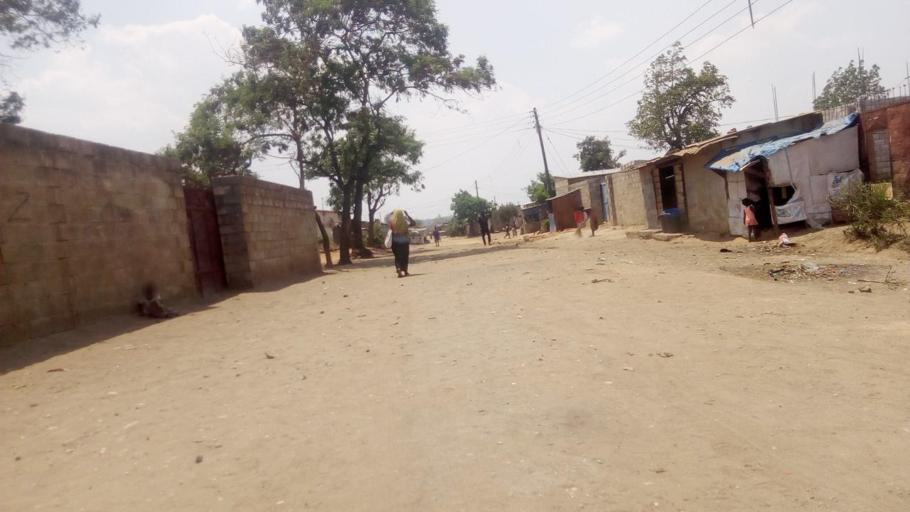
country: ZM
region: Lusaka
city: Lusaka
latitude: -15.3654
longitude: 28.2927
